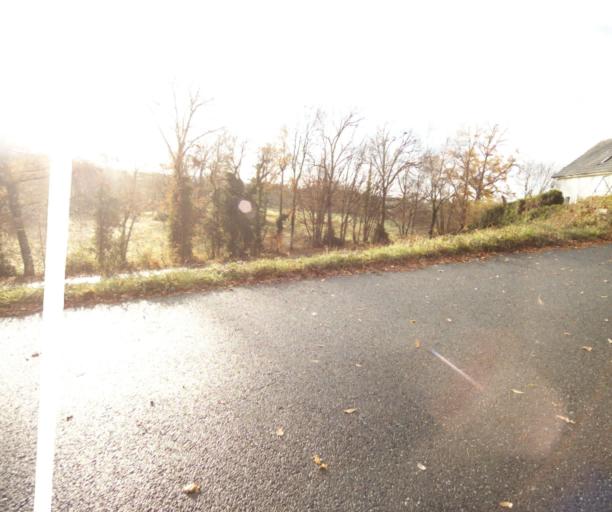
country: FR
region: Limousin
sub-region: Departement de la Correze
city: Saint-Mexant
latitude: 45.2669
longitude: 1.6433
